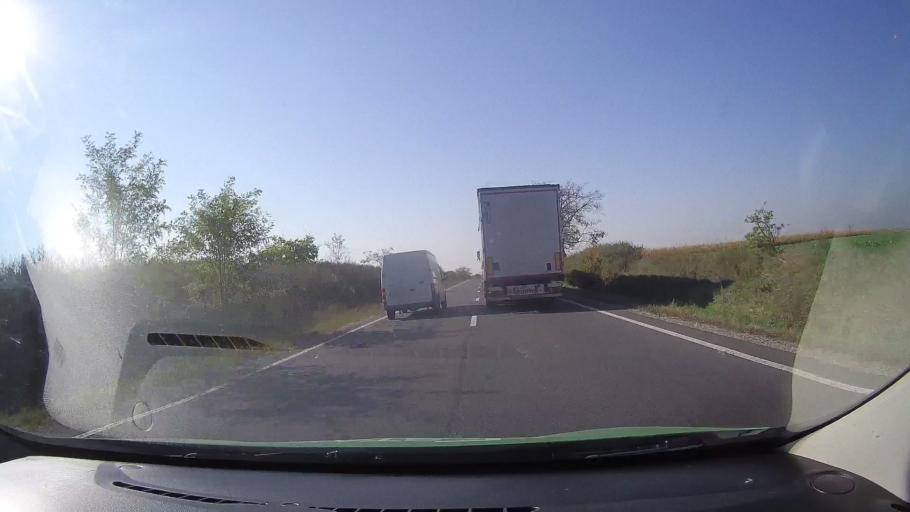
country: RO
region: Satu Mare
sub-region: Comuna Petresti
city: Petresti
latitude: 47.6326
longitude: 22.3957
